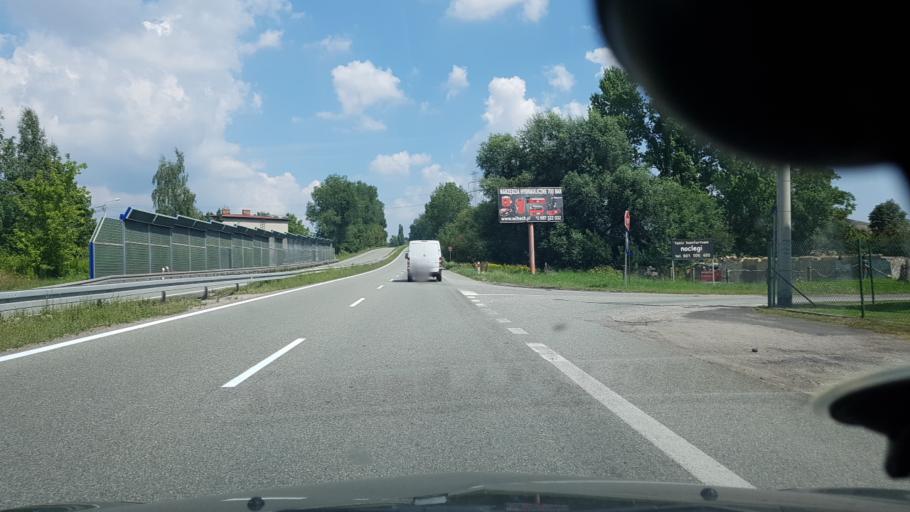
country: PL
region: Silesian Voivodeship
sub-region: Powiat mikolowski
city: Laziska Gorne
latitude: 50.1382
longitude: 18.8355
